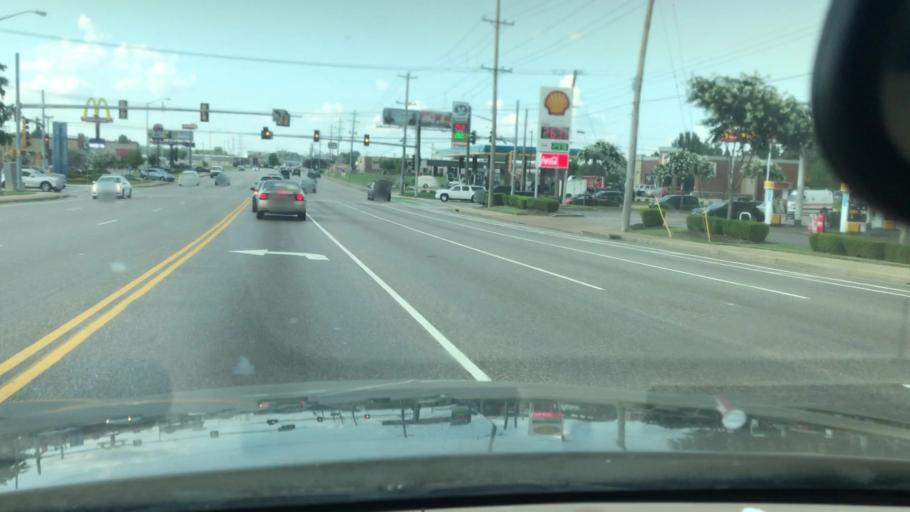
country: US
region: Tennessee
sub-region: Shelby County
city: Bartlett
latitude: 35.1778
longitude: -89.8362
